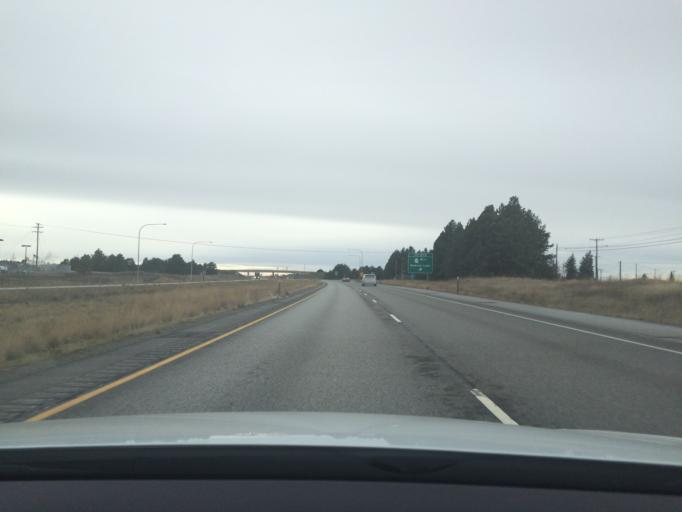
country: US
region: Washington
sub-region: Spokane County
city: Airway Heights
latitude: 47.5957
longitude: -117.5600
